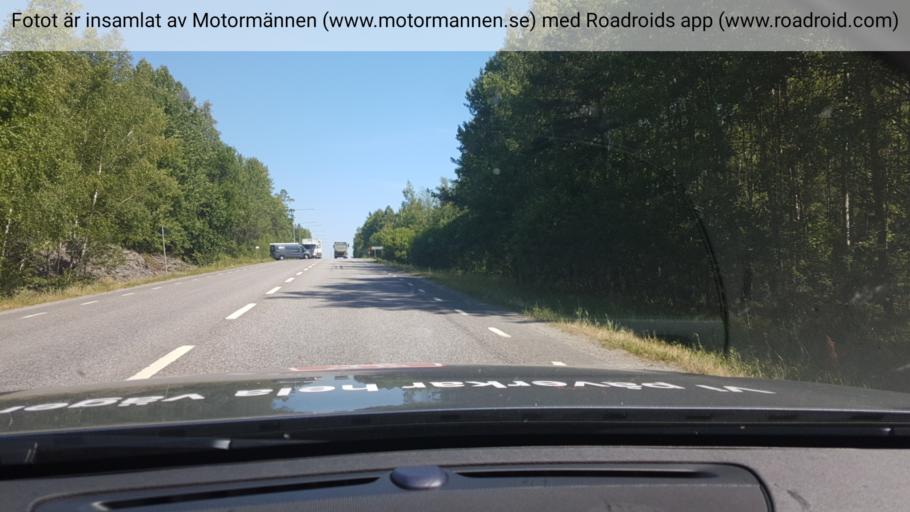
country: SE
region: Stockholm
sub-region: Haninge Kommun
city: Handen
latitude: 59.1953
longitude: 18.1198
